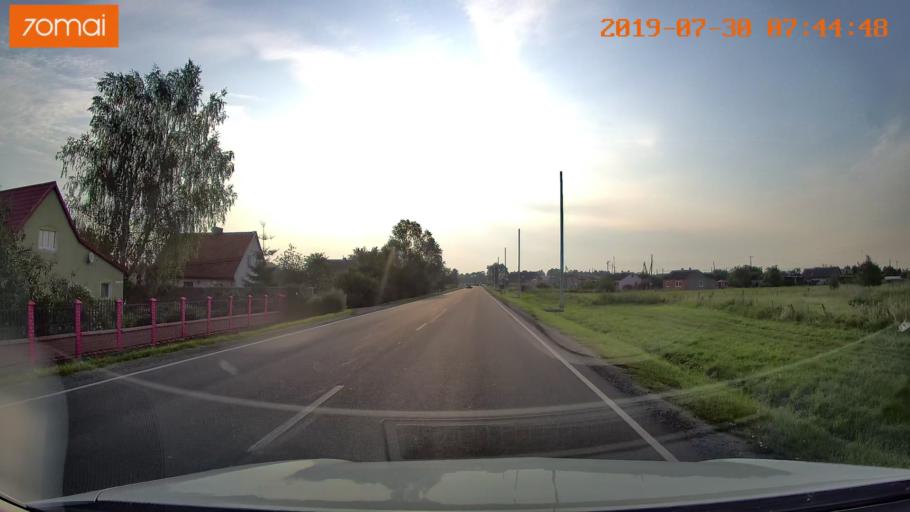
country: RU
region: Kaliningrad
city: Gvardeysk
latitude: 54.6504
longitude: 21.3339
